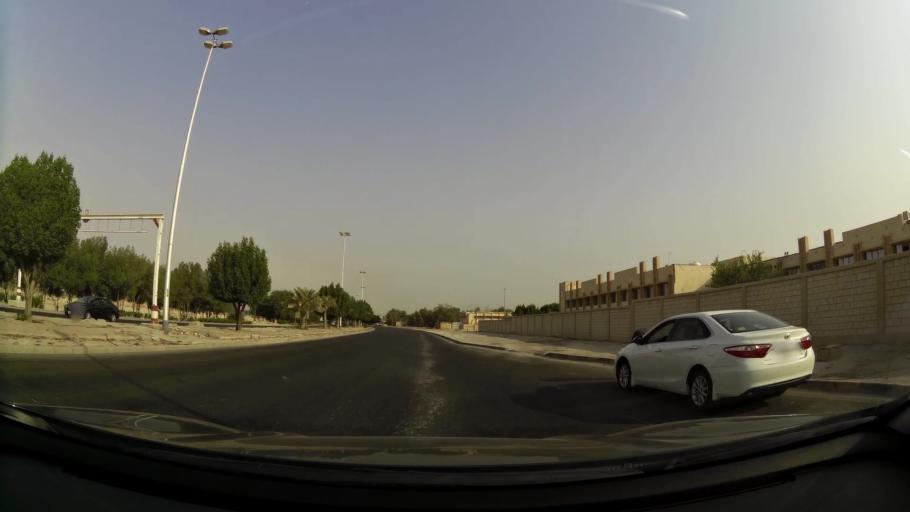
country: KW
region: Al Asimah
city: Ar Rabiyah
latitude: 29.3131
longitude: 47.8063
